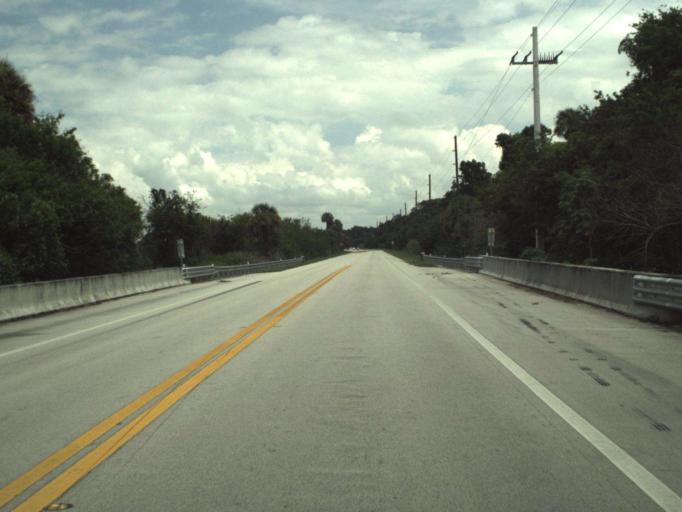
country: US
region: Florida
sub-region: Okeechobee County
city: Taylor Creek
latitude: 27.1063
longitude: -80.6610
